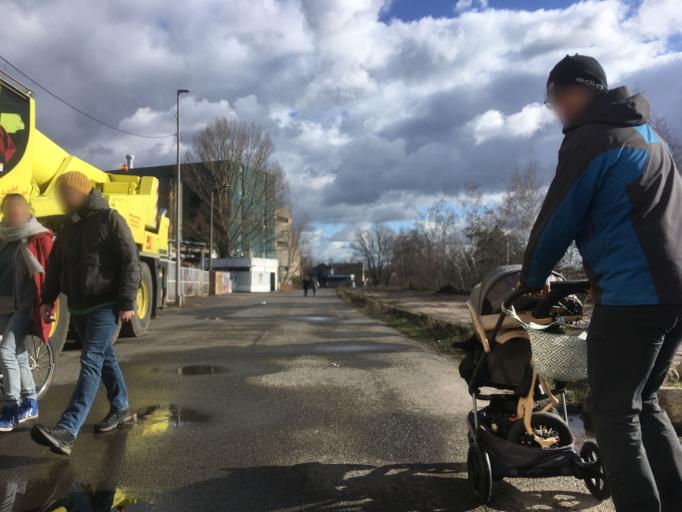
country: DE
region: Berlin
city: Oberschoneweide
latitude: 52.4556
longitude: 13.5299
